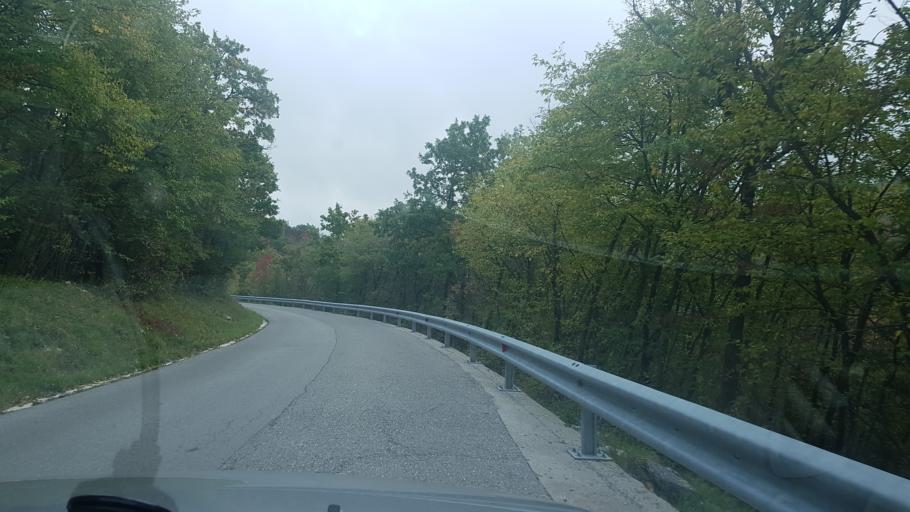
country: SI
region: Hrpelje-Kozina
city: Kozina
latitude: 45.5174
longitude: 13.9579
